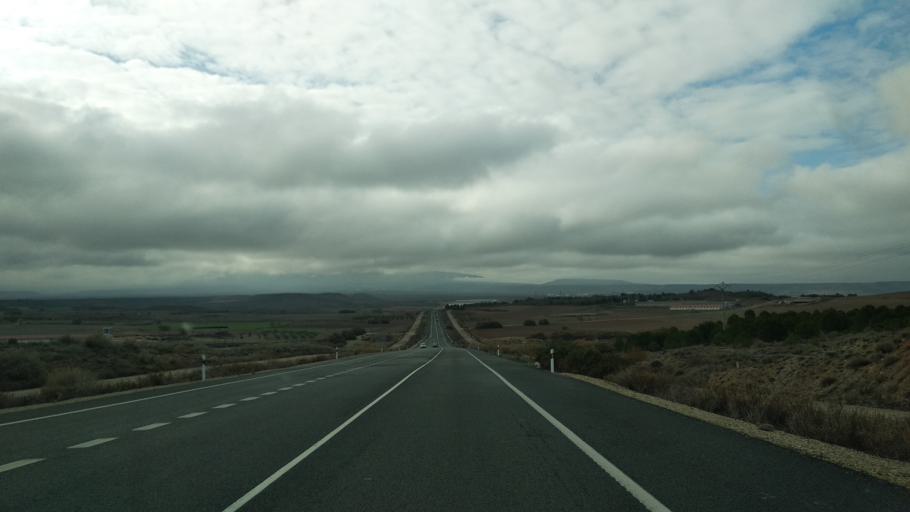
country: ES
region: La Rioja
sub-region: Provincia de La Rioja
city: Pradejon
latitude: 42.3210
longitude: -2.0221
